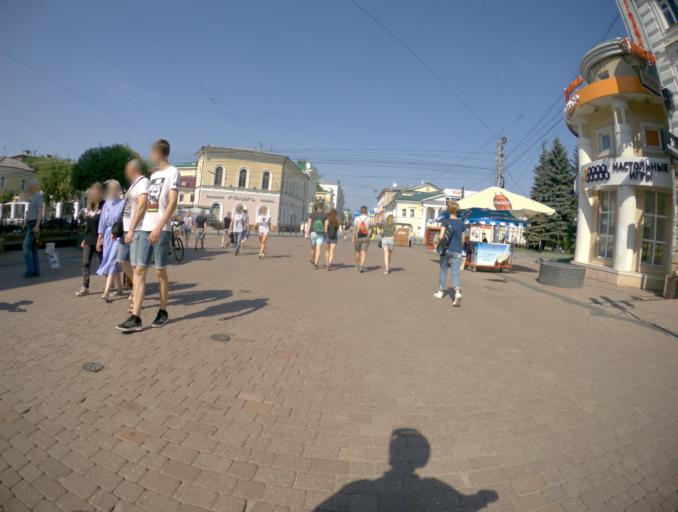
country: RU
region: Nizjnij Novgorod
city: Nizhniy Novgorod
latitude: 56.3215
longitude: 43.9997
